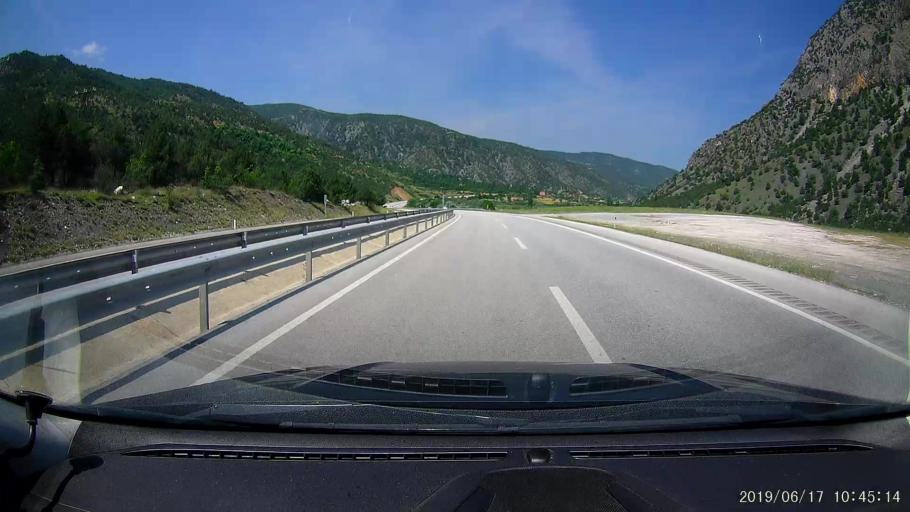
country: TR
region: Corum
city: Hacihamza
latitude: 41.0644
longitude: 34.4948
